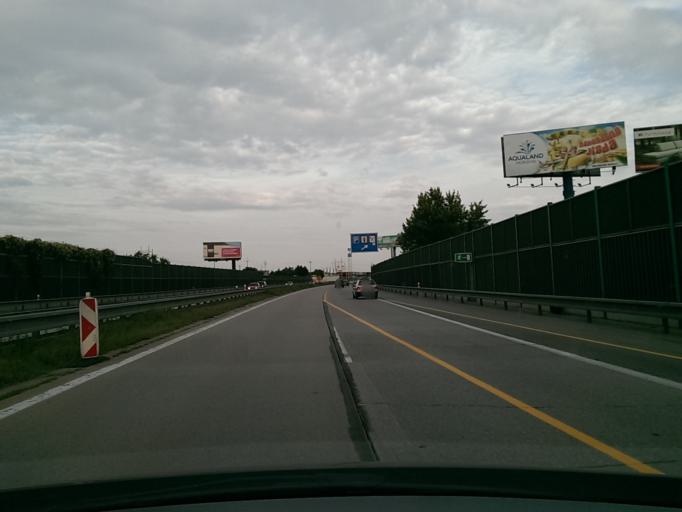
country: CZ
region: South Moravian
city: Troubsko
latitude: 49.1754
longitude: 16.5054
